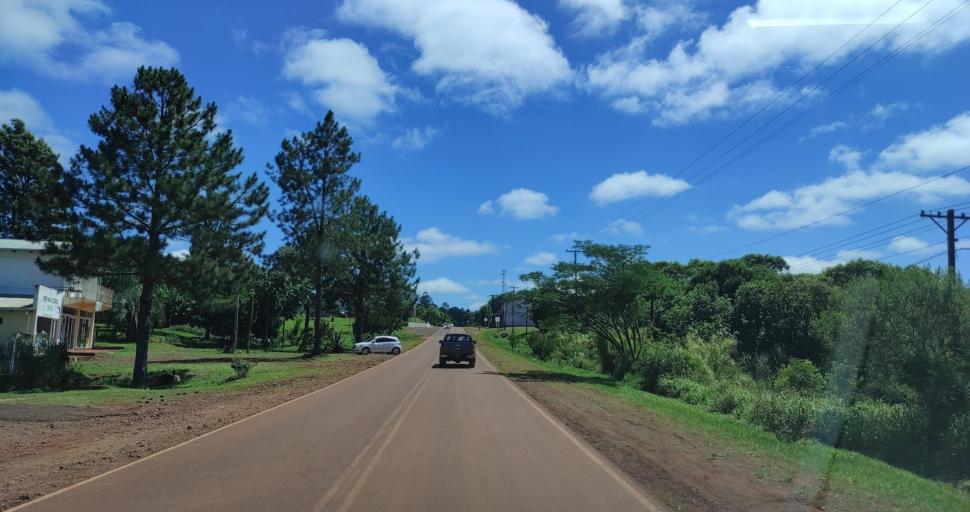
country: AR
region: Misiones
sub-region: Departamento de Veinticinco de Mayo
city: Veinticinco de Mayo
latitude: -27.3890
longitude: -54.7474
